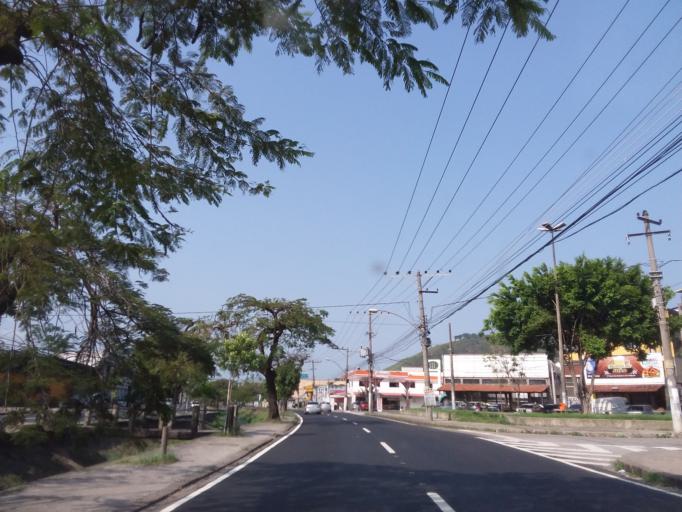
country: BR
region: Rio de Janeiro
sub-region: Nilopolis
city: Nilopolis
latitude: -22.9015
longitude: -43.5445
